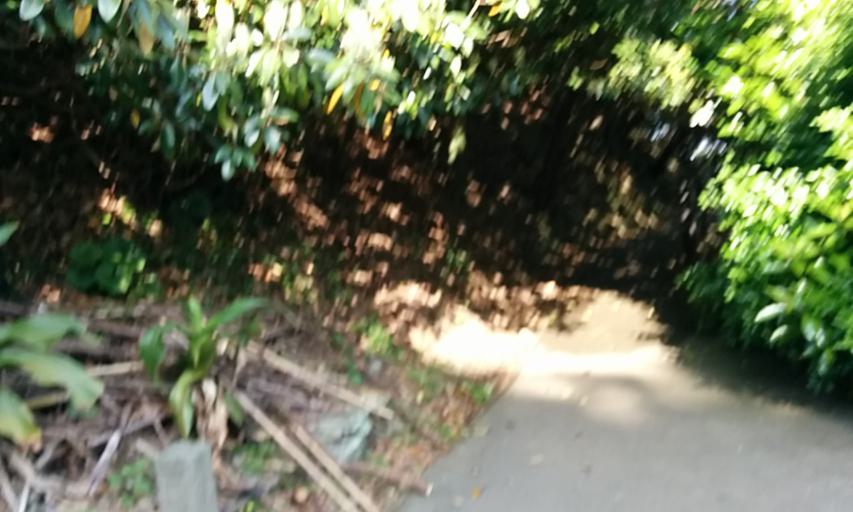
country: JP
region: Oita
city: Tsukumiura
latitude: 33.3461
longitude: 132.0214
